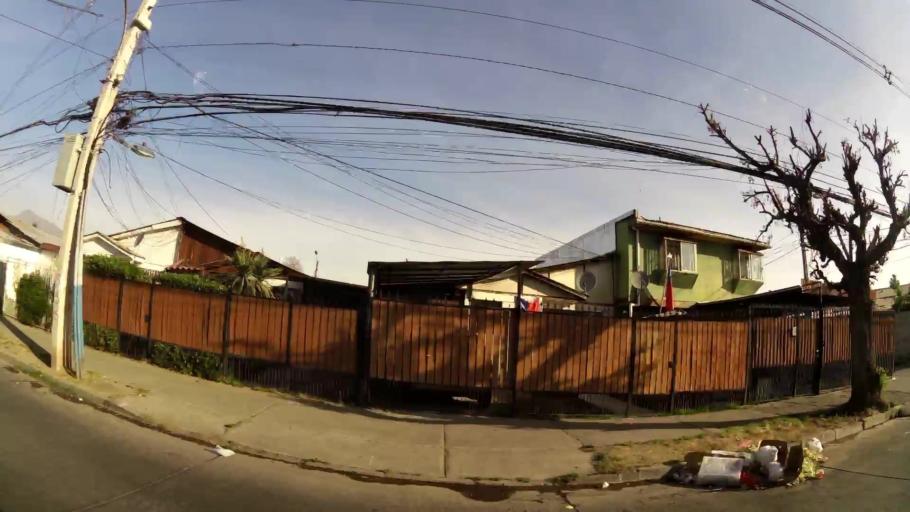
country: CL
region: Santiago Metropolitan
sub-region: Provincia de Cordillera
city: Puente Alto
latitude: -33.5527
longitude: -70.5692
